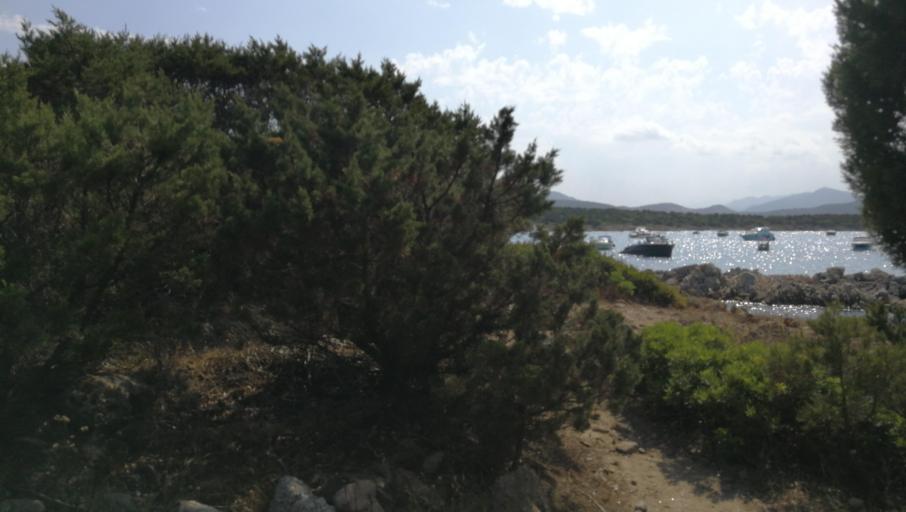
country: IT
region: Sardinia
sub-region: Provincia di Olbia-Tempio
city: Golfo Aranci
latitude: 41.0138
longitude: 9.5871
